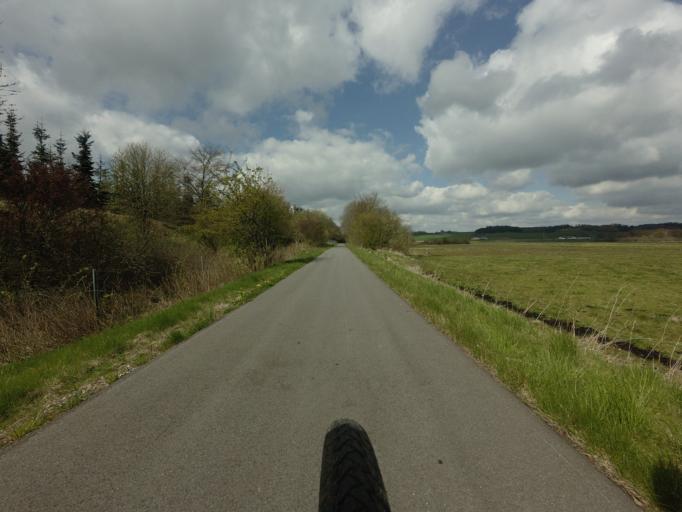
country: DK
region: North Denmark
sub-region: Mariagerfjord Kommune
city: Hadsund
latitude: 56.8453
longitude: 10.1052
